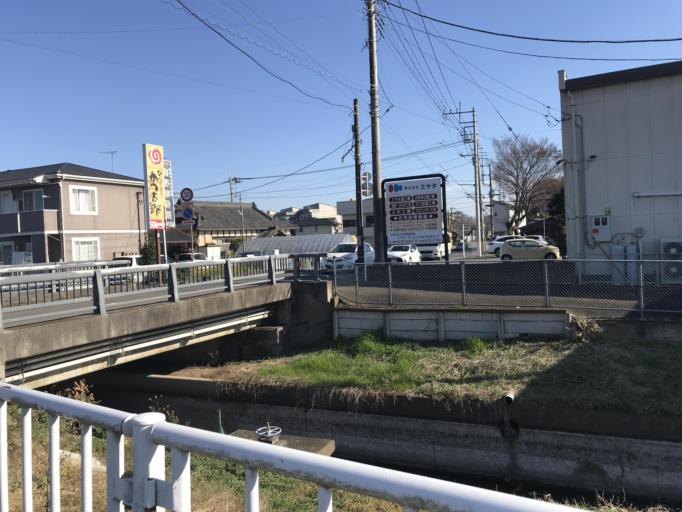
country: JP
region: Ibaraki
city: Yuki
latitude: 36.2878
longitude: 139.8605
